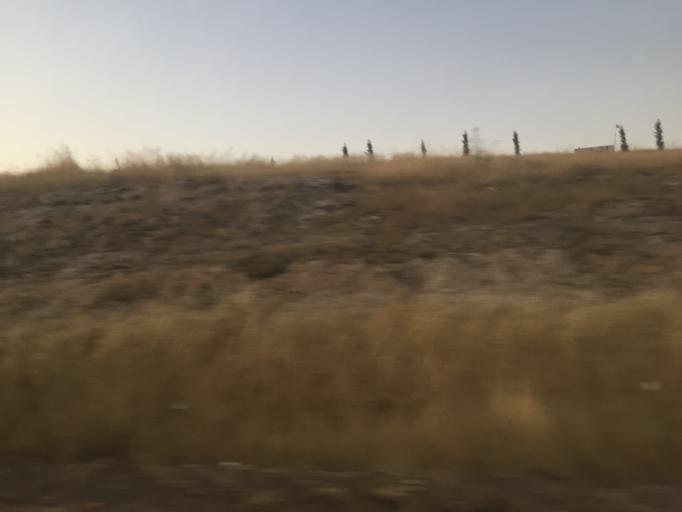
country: TR
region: Mardin
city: Kindirip
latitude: 37.4632
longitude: 41.2289
